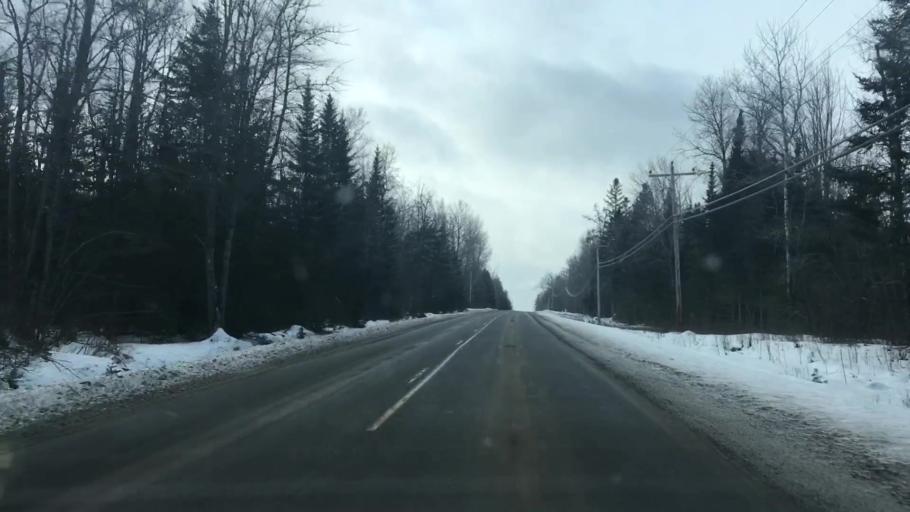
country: US
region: Maine
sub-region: Washington County
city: Calais
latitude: 45.0398
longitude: -67.3305
